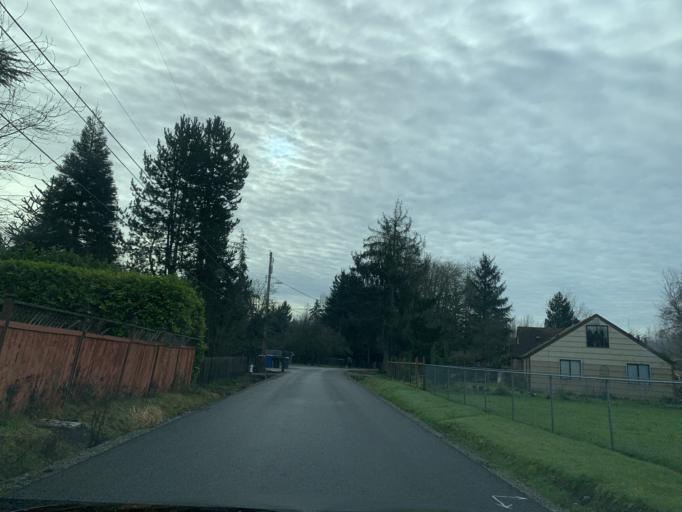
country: US
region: Washington
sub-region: Pierce County
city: Fife Heights
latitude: 47.2561
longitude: -122.3528
